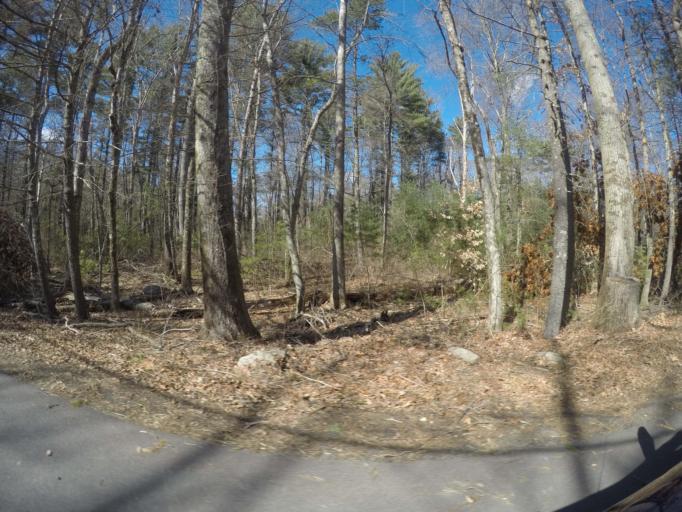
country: US
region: Massachusetts
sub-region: Bristol County
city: Easton
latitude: 41.9958
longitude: -71.1071
